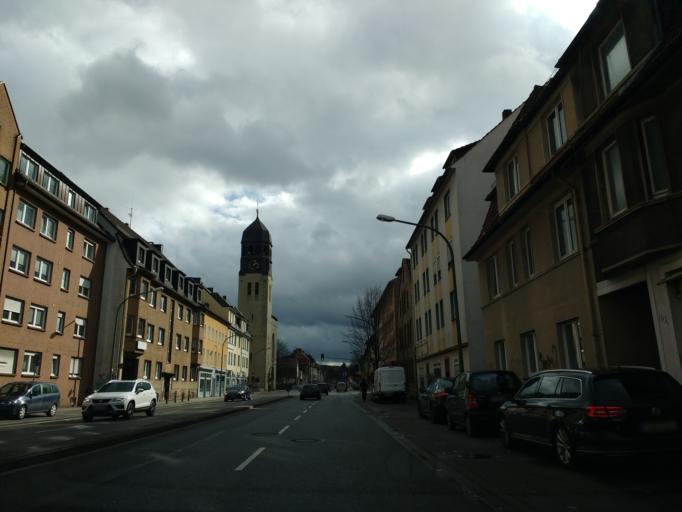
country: DE
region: Lower Saxony
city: Osnabrueck
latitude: 52.2617
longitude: 8.0559
